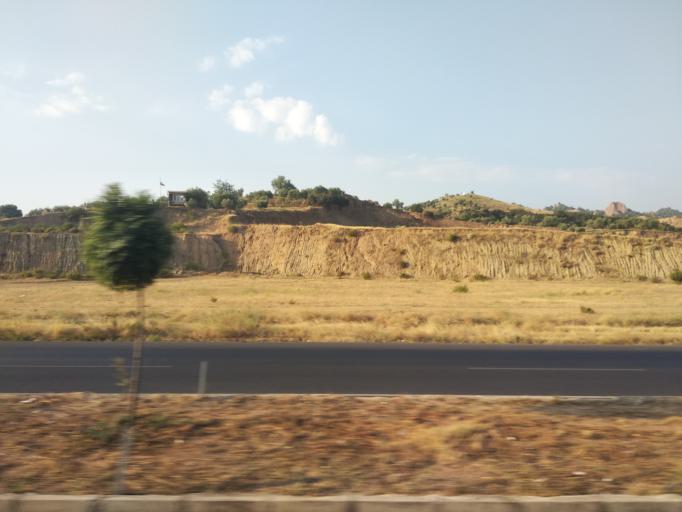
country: TR
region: Manisa
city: Ahmetli
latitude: 38.5100
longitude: 27.9766
